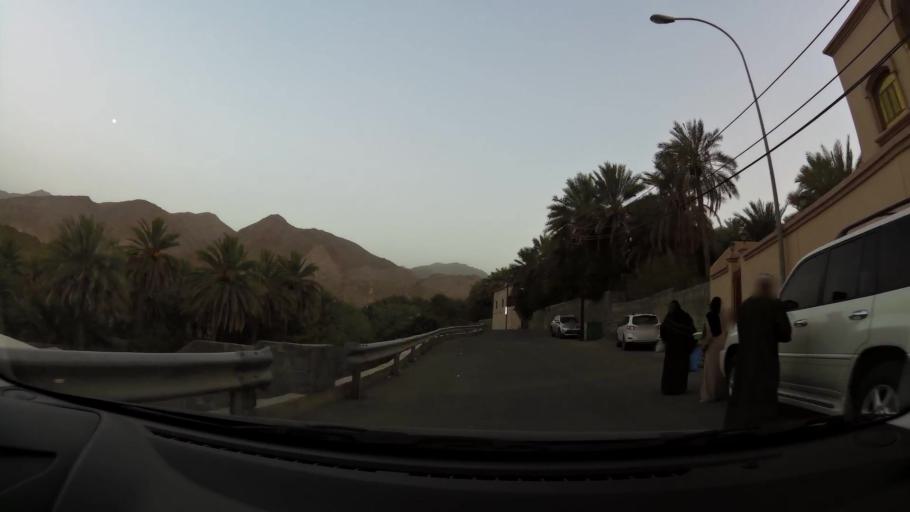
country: OM
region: Muhafazat Masqat
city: Bawshar
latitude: 23.4820
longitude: 58.3283
